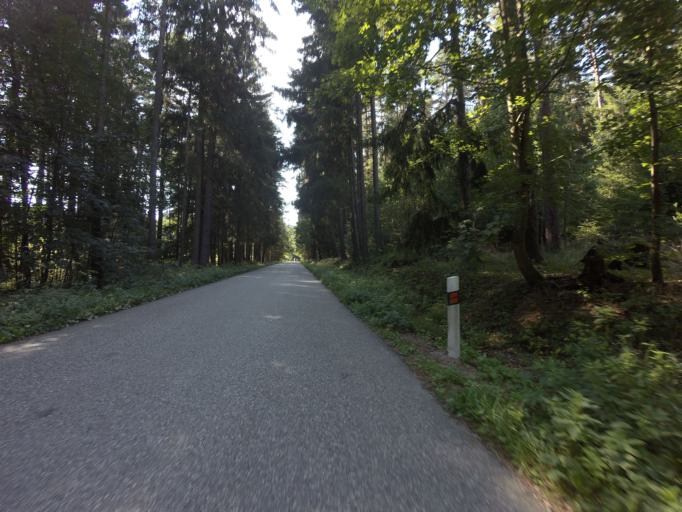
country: CZ
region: Jihocesky
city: Tyn nad Vltavou
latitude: 49.1558
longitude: 14.4356
